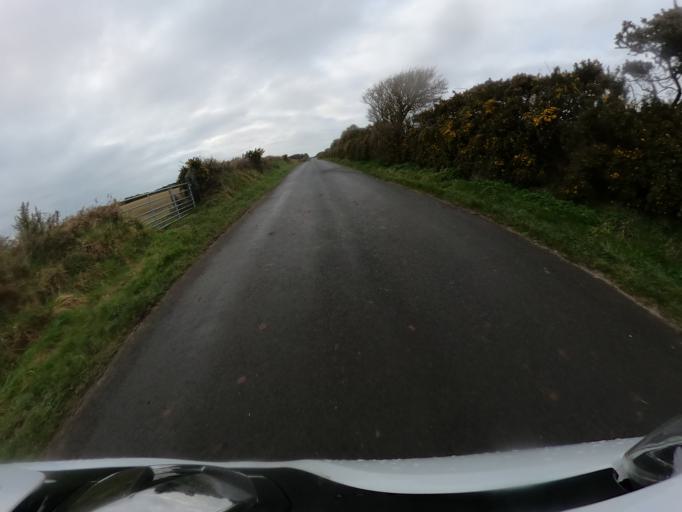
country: IM
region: Ramsey
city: Ramsey
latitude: 54.3488
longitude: -4.5230
